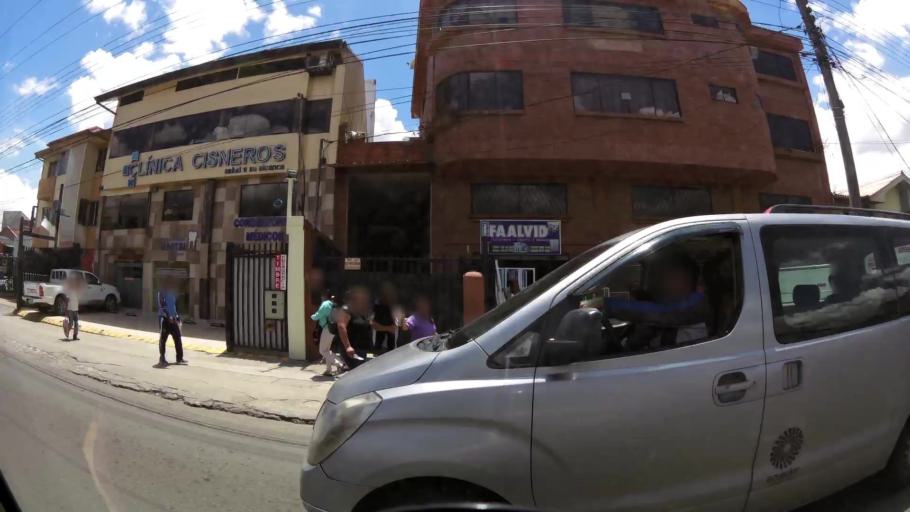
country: EC
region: Azuay
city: Cuenca
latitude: -2.9015
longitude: -79.0287
